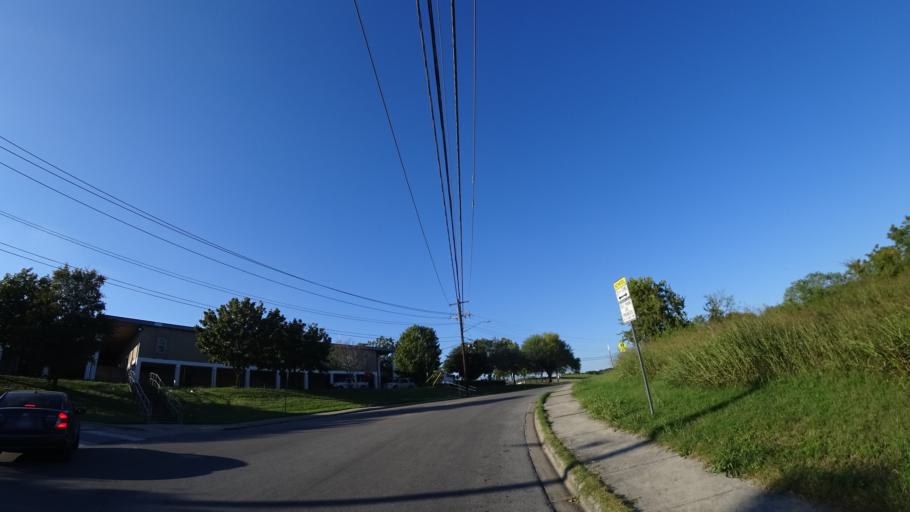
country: US
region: Texas
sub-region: Travis County
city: Austin
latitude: 30.2239
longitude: -97.7371
